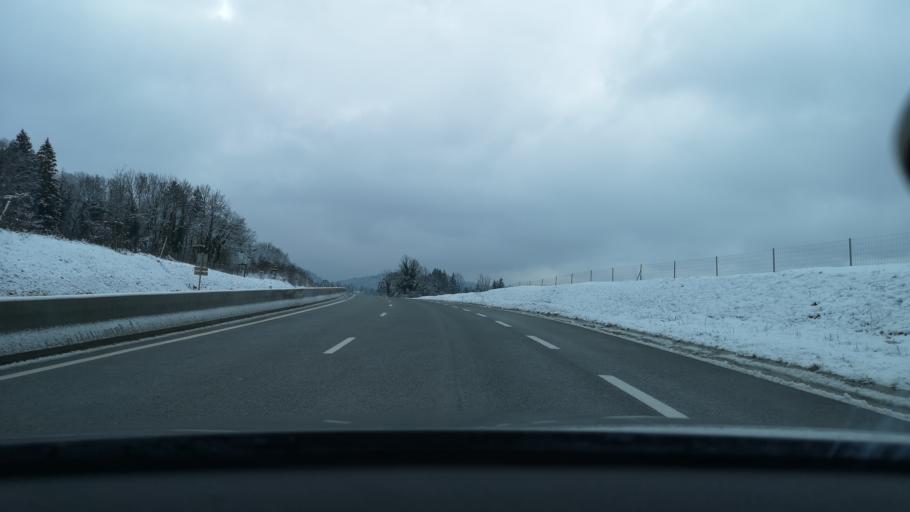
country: FR
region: Rhone-Alpes
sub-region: Departement de l'Ain
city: Dortan
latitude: 46.3179
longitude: 5.6711
